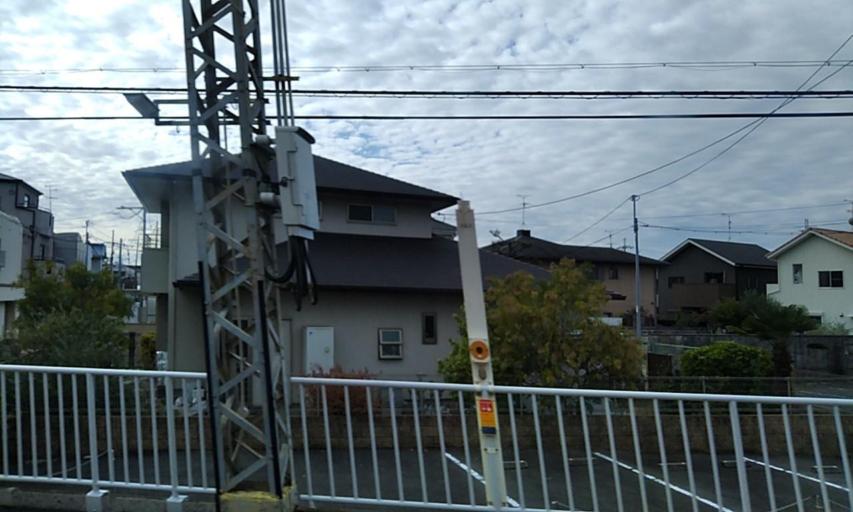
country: JP
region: Osaka
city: Matsubara
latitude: 34.5739
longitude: 135.5721
